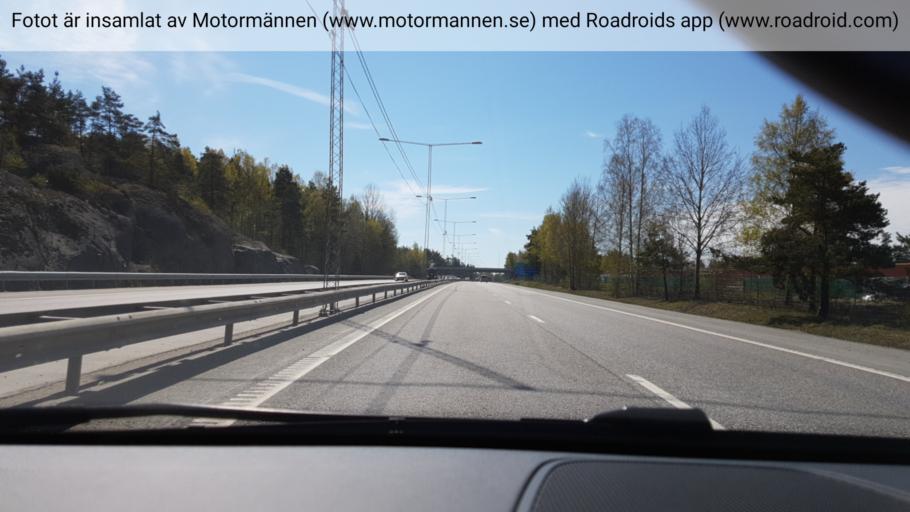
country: SE
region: Stockholm
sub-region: Haninge Kommun
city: Haninge
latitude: 59.1714
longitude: 18.1589
